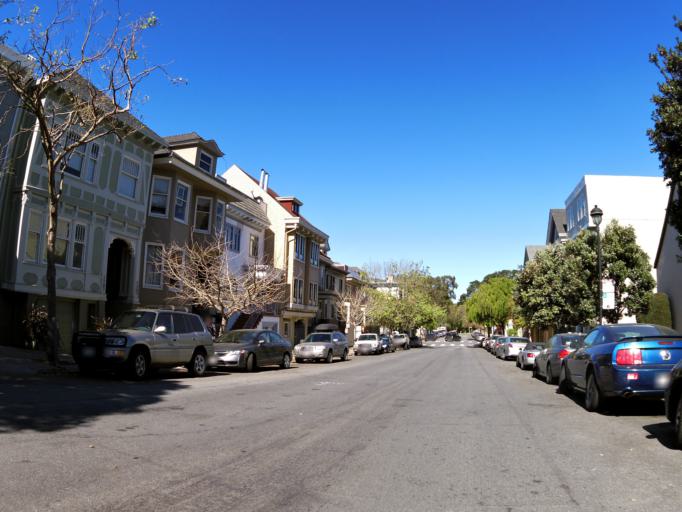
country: US
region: California
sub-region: San Francisco County
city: San Francisco
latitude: 37.7645
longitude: -122.4621
